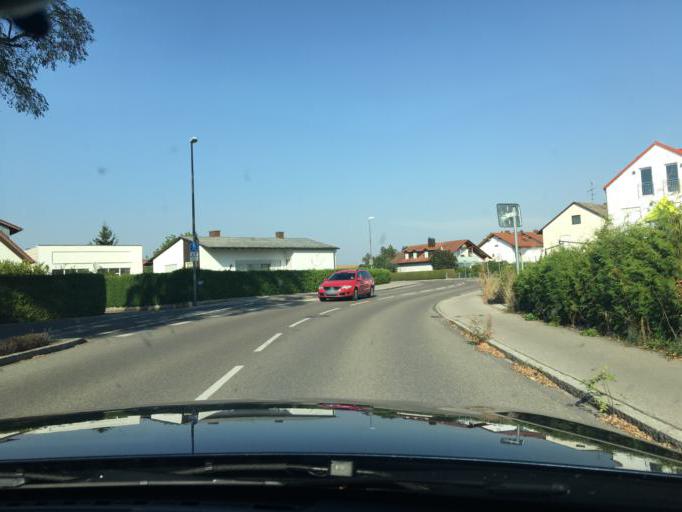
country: DE
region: Bavaria
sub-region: Upper Bavaria
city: Gaimersheim
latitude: 48.7937
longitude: 11.3782
